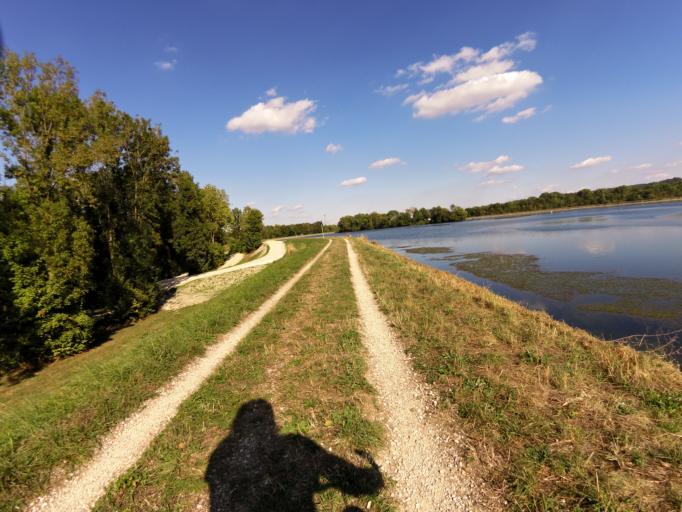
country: DE
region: Bavaria
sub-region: Lower Bavaria
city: Stallwang
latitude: 48.5803
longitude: 12.2110
